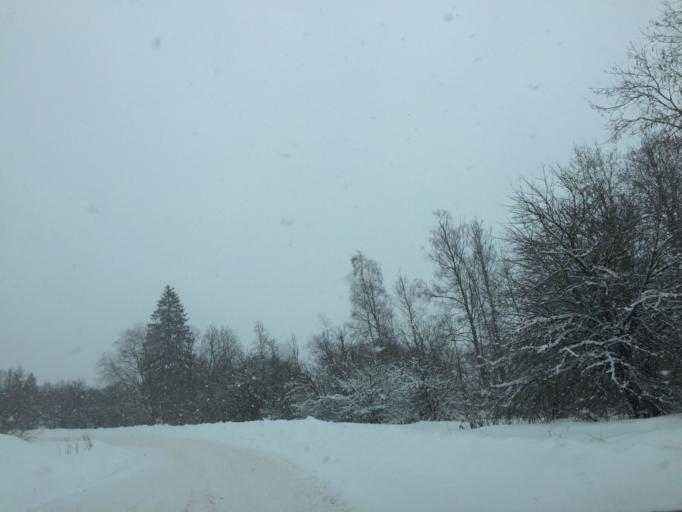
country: LV
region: Amatas Novads
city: Drabesi
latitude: 57.0677
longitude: 25.3226
